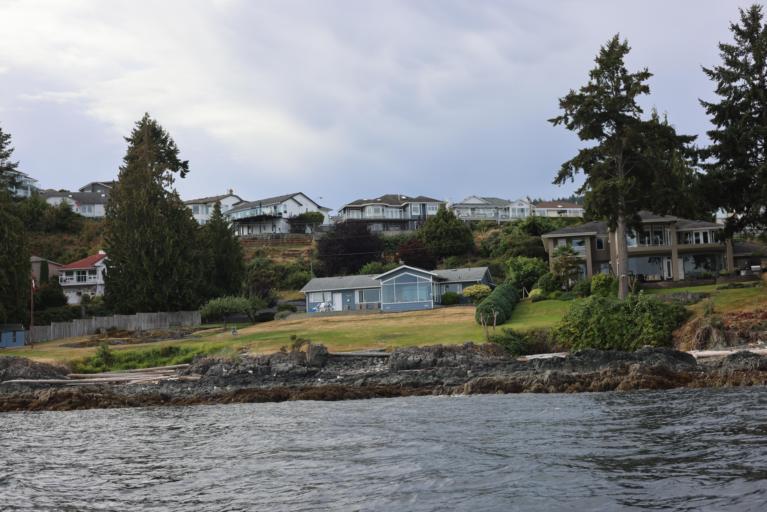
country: CA
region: British Columbia
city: Nanaimo
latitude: 49.2401
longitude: -123.9887
